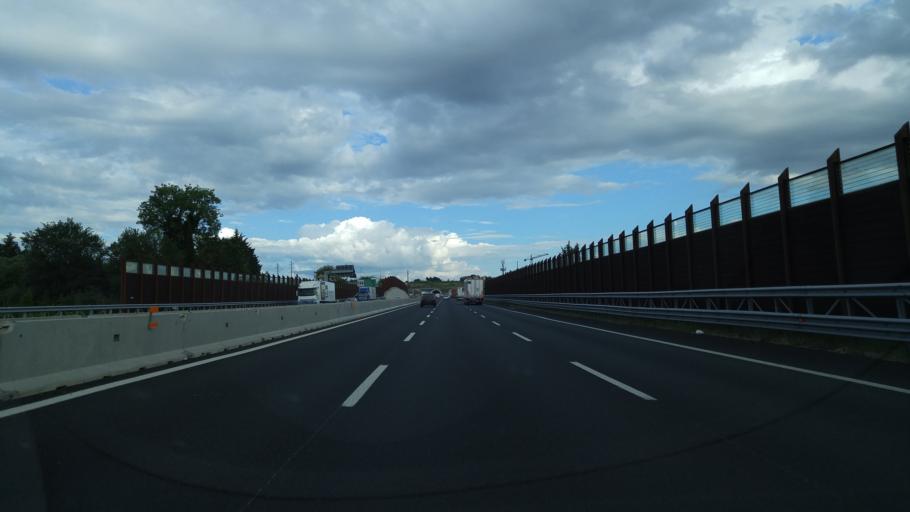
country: IT
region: Emilia-Romagna
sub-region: Provincia di Rimini
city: Riccione
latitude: 43.9839
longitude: 12.6441
